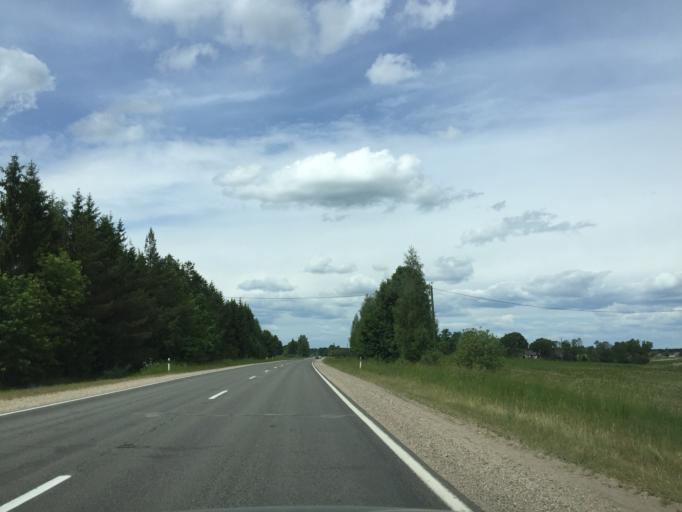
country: LV
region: Vilanu
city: Vilani
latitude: 56.5866
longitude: 26.8863
